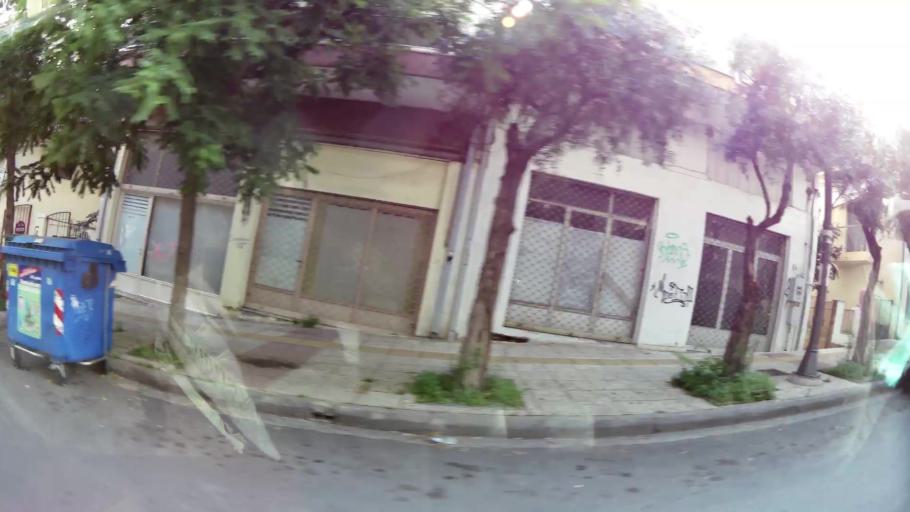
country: GR
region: Central Macedonia
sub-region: Nomos Thessalonikis
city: Sykies
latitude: 40.6483
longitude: 22.9482
